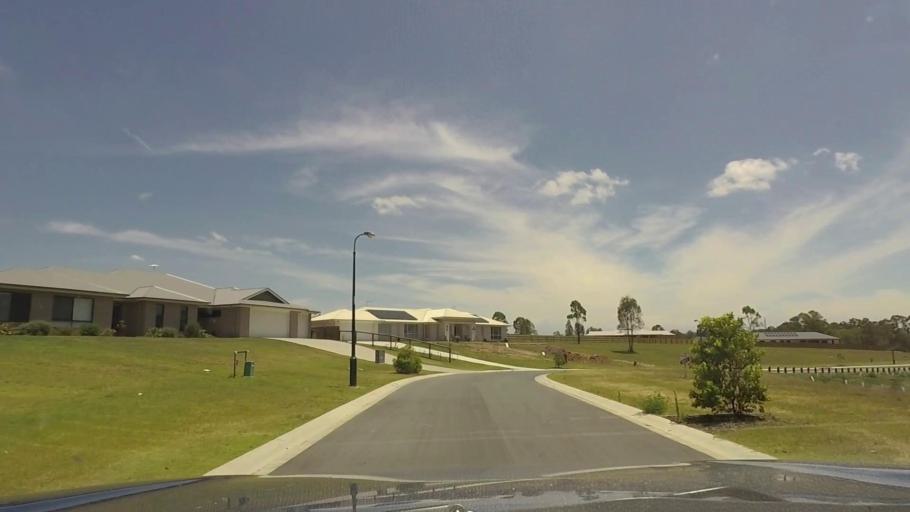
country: AU
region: Queensland
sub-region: Logan
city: Chambers Flat
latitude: -27.7695
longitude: 153.0896
